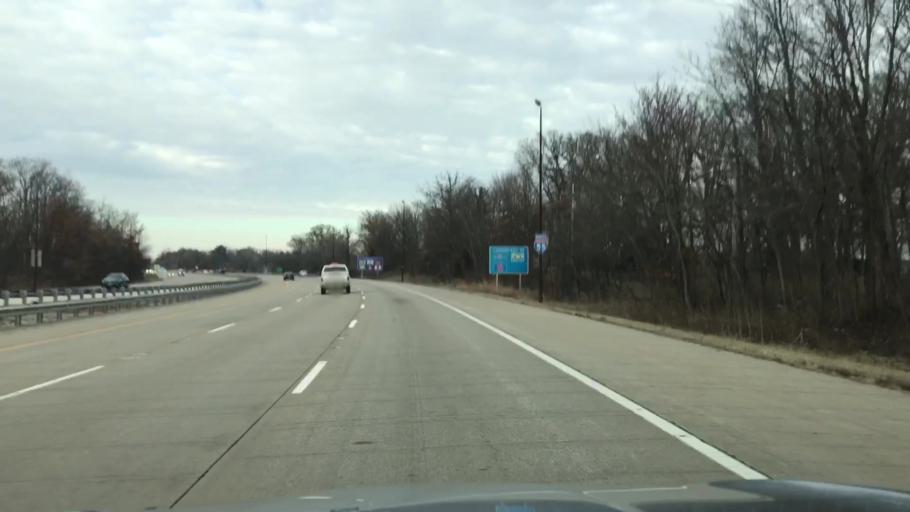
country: US
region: Illinois
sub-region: Sangamon County
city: Chatham
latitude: 39.6922
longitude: -89.6422
